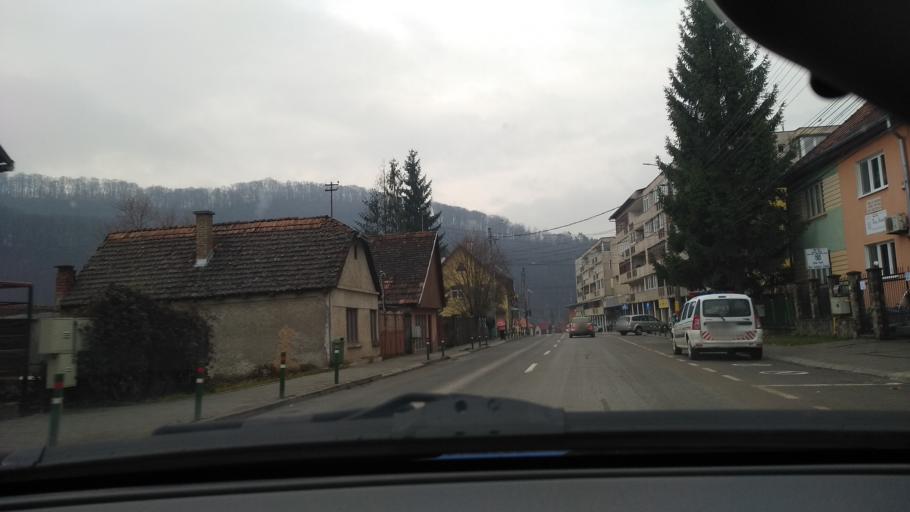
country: RO
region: Mures
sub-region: Oras Sovata
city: Sovata
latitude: 46.5954
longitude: 25.0718
